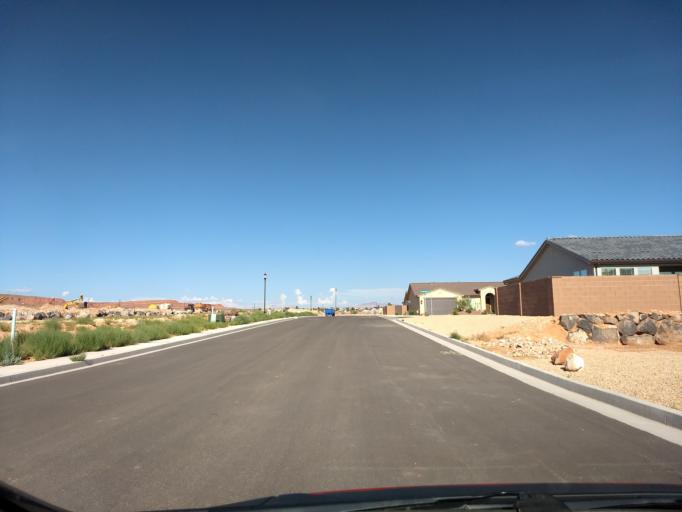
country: US
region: Utah
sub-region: Washington County
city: Washington
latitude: 37.1452
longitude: -113.5178
